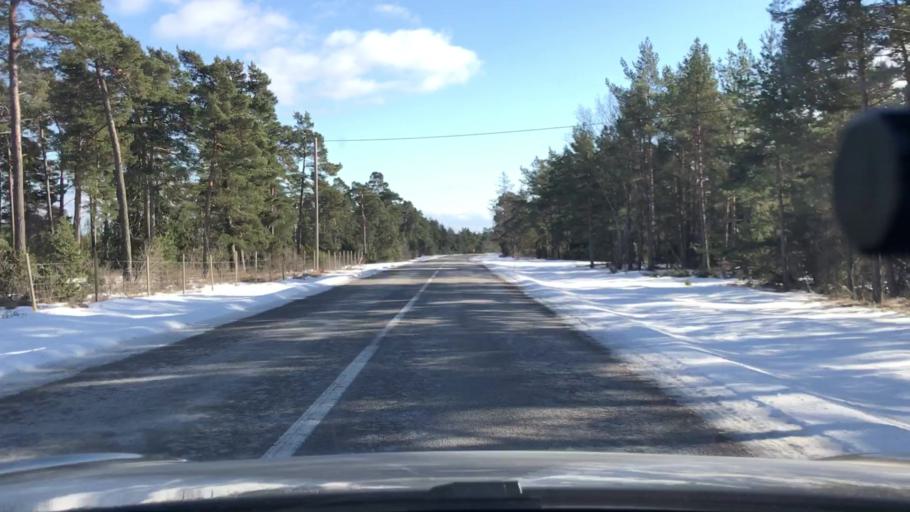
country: SE
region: Gotland
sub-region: Gotland
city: Hemse
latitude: 57.3487
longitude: 18.6898
